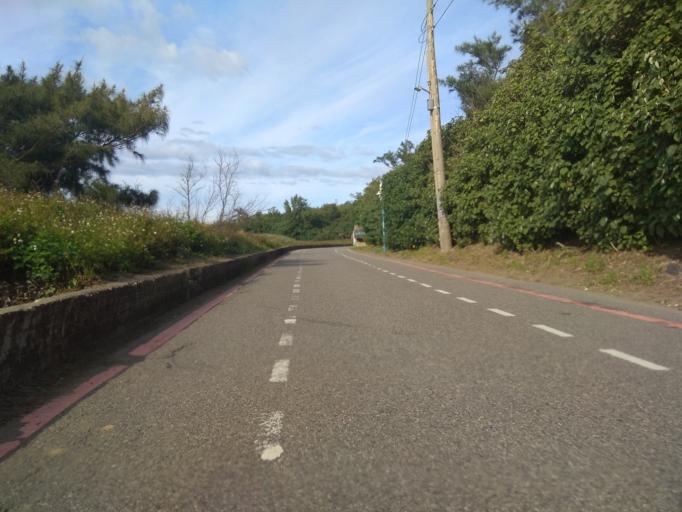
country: TW
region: Taiwan
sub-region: Hsinchu
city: Zhubei
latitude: 24.9796
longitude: 121.0161
